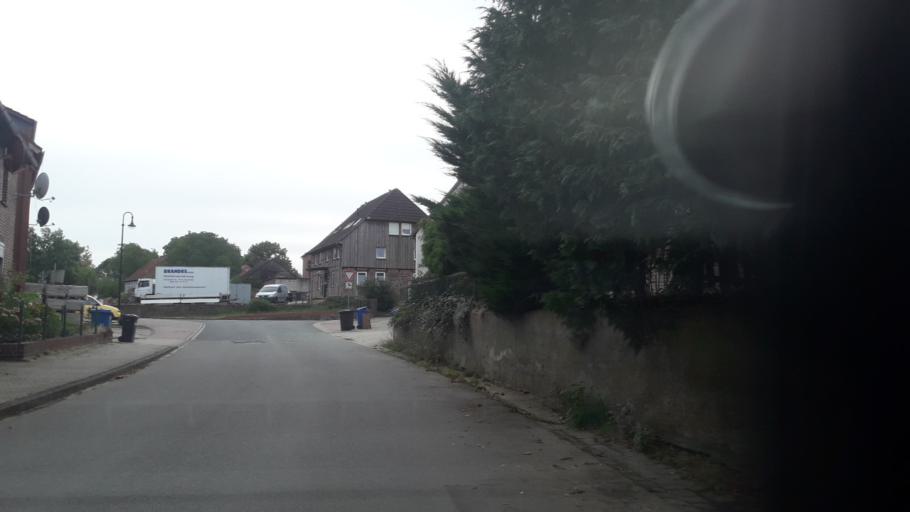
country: DE
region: Lower Saxony
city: Gross Twulpstedt
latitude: 52.3639
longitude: 10.8853
